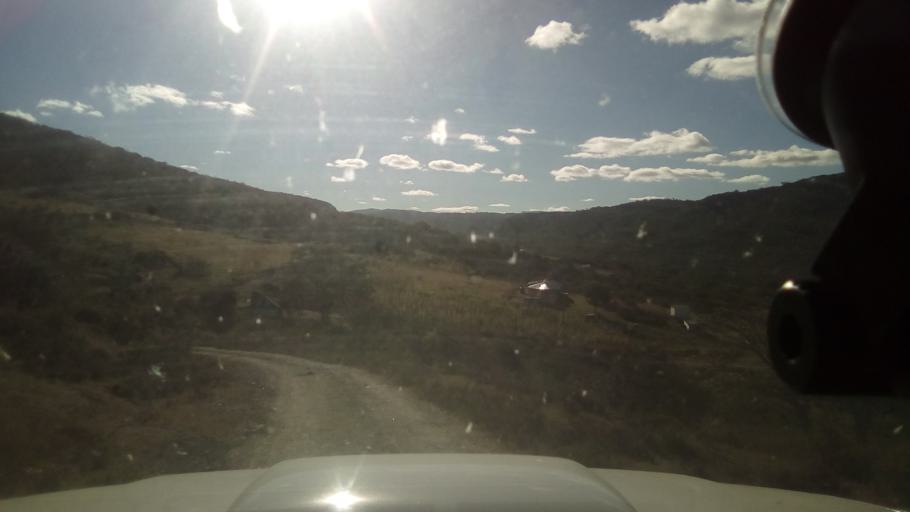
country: ZA
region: Eastern Cape
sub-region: Buffalo City Metropolitan Municipality
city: Bhisho
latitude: -32.7331
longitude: 27.3478
